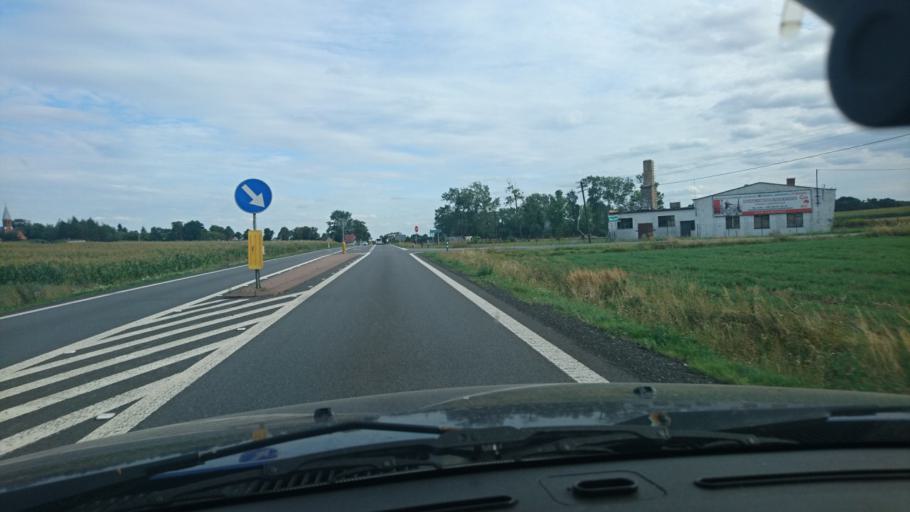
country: PL
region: Greater Poland Voivodeship
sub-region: Powiat ostrzeszowski
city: Ostrzeszow
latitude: 51.3900
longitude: 17.9460
